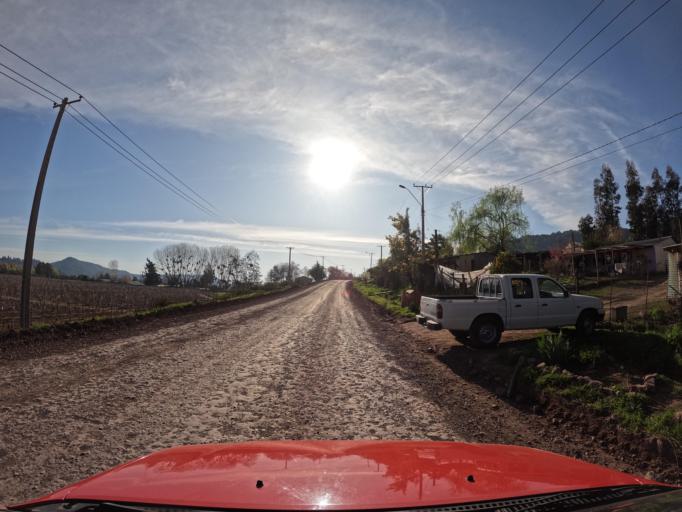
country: CL
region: Maule
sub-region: Provincia de Curico
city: Teno
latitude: -34.9659
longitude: -70.9494
